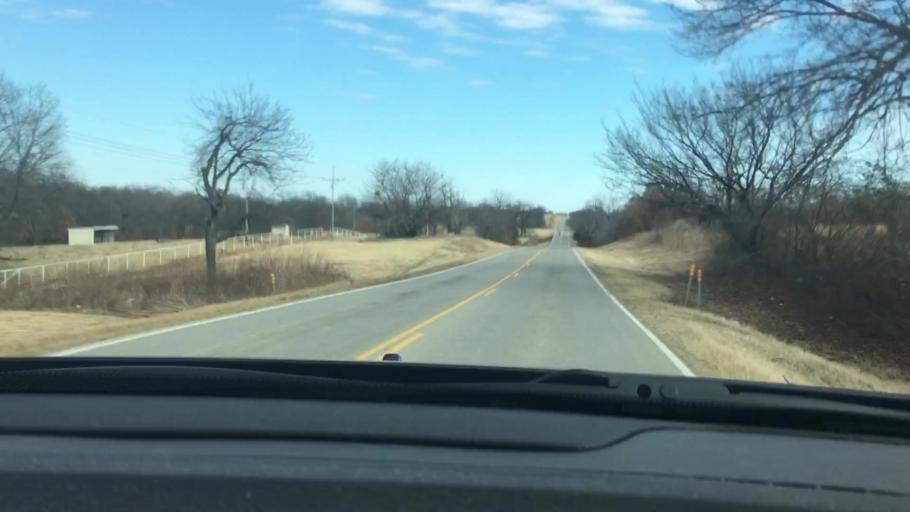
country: US
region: Oklahoma
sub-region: Garvin County
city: Stratford
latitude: 34.7972
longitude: -96.8442
